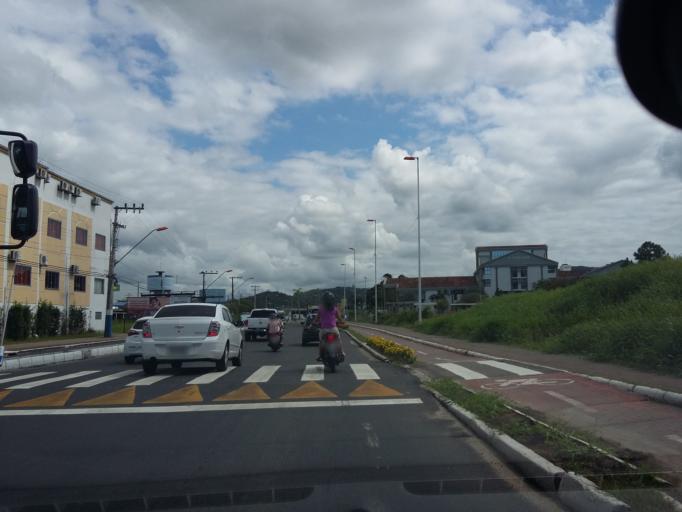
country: BR
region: Santa Catarina
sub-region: Balneario Camboriu
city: Balneario Camboriu
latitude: -26.9942
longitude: -48.6515
